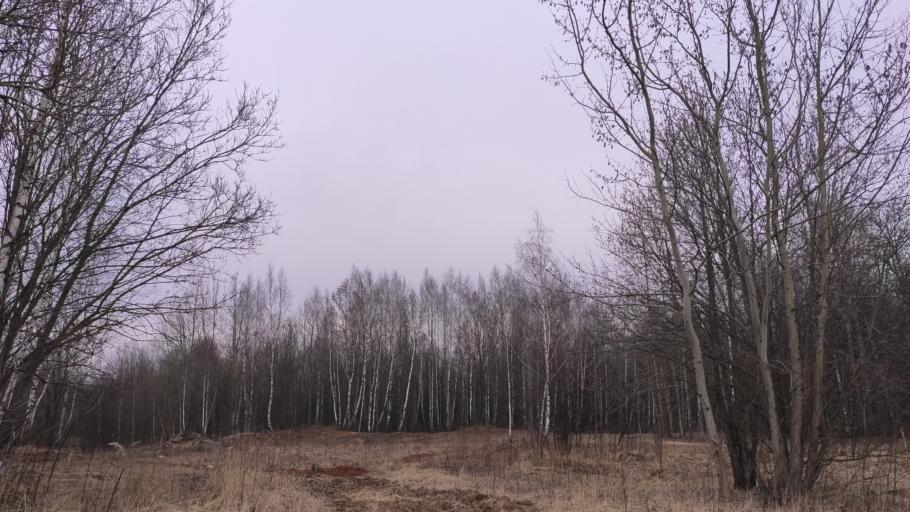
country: BY
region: Minsk
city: Novoye Medvezhino
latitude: 53.8896
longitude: 27.4695
